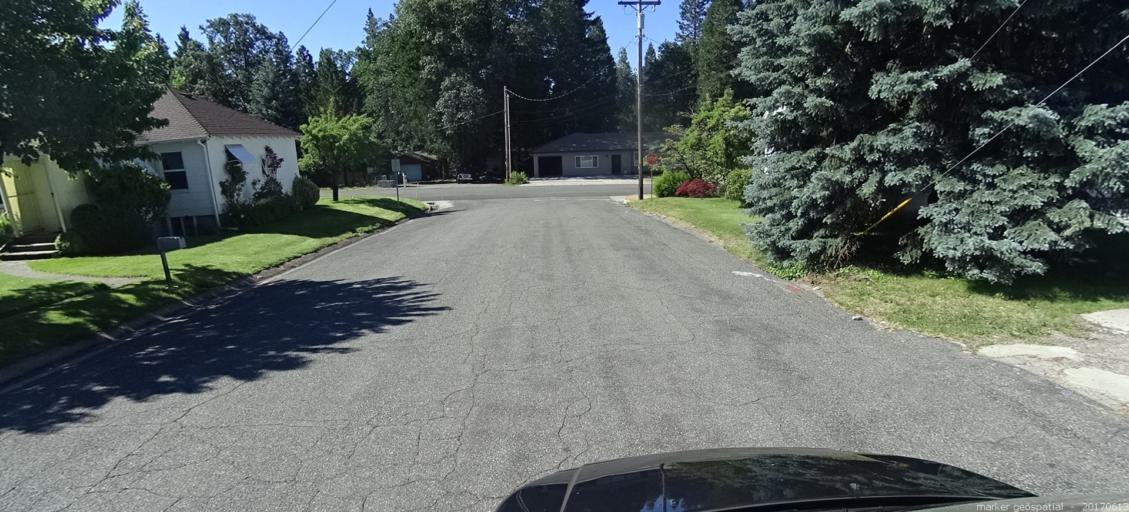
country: US
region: California
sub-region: Siskiyou County
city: Mount Shasta
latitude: 41.3056
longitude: -122.3080
